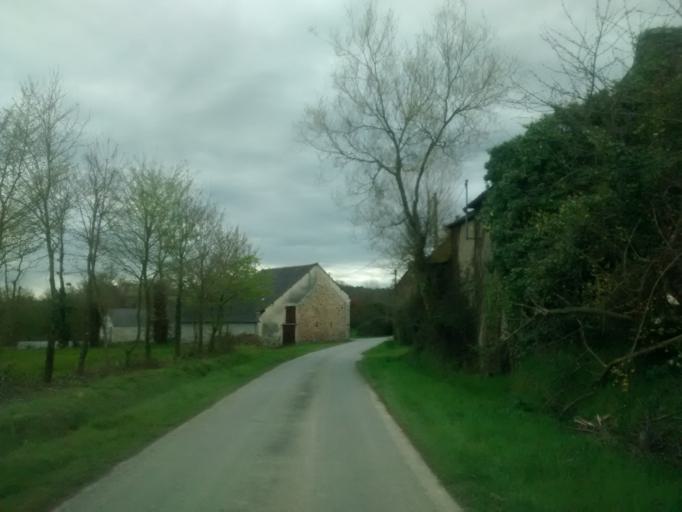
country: FR
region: Brittany
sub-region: Departement d'Ille-et-Vilaine
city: Erce-pres-Liffre
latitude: 48.2397
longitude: -1.4978
